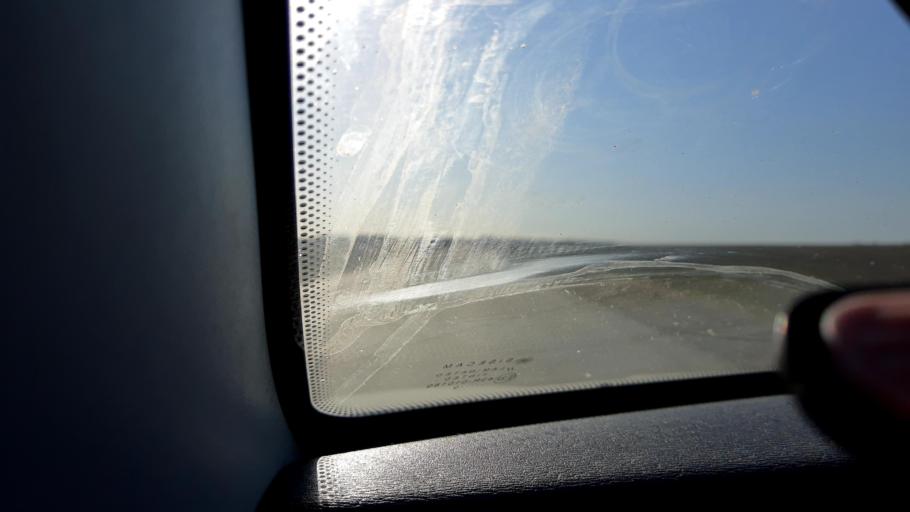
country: RU
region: Bashkortostan
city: Avdon
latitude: 54.8227
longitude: 55.6699
